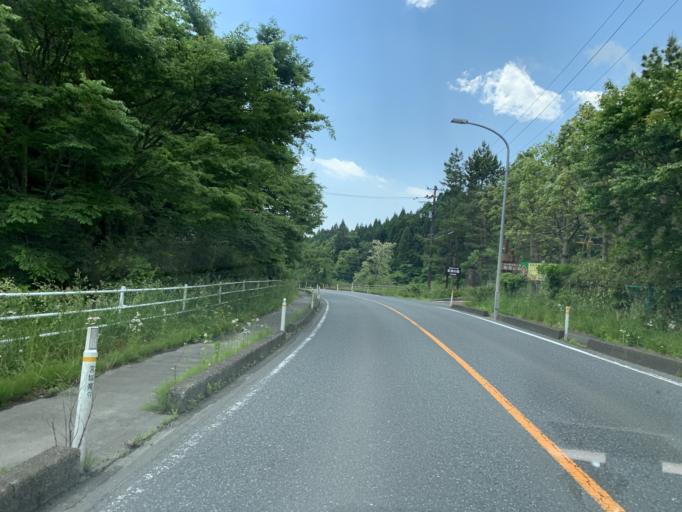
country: JP
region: Miyagi
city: Matsushima
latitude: 38.4100
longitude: 141.0636
